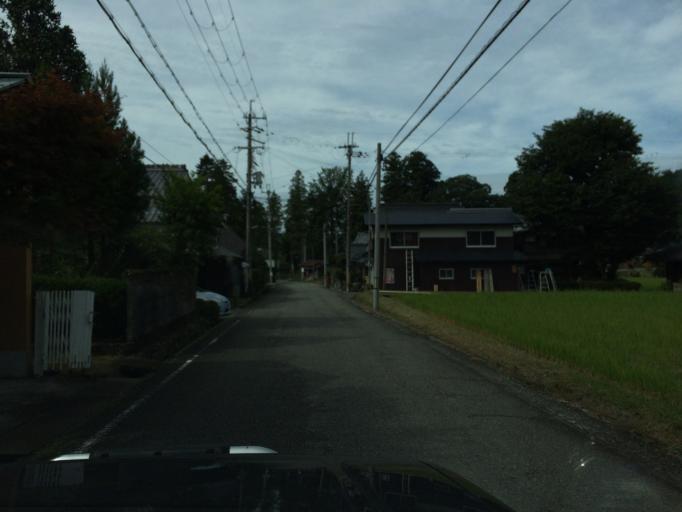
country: JP
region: Hyogo
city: Sasayama
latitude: 35.0722
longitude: 135.3521
